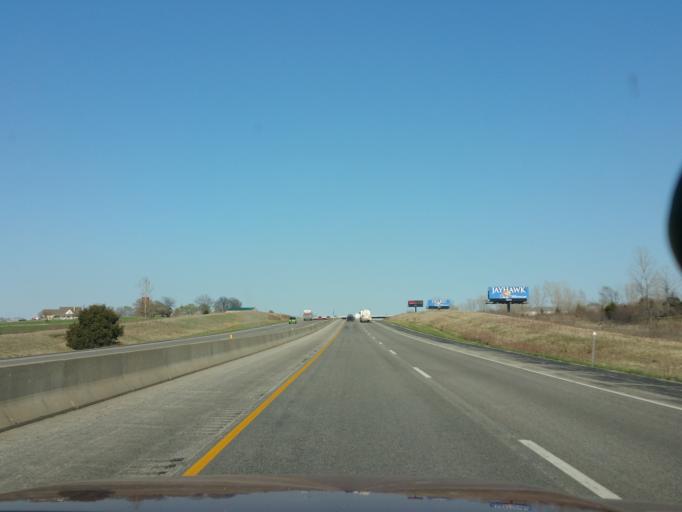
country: US
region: Kansas
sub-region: Leavenworth County
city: Basehor
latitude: 39.0817
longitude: -94.9529
